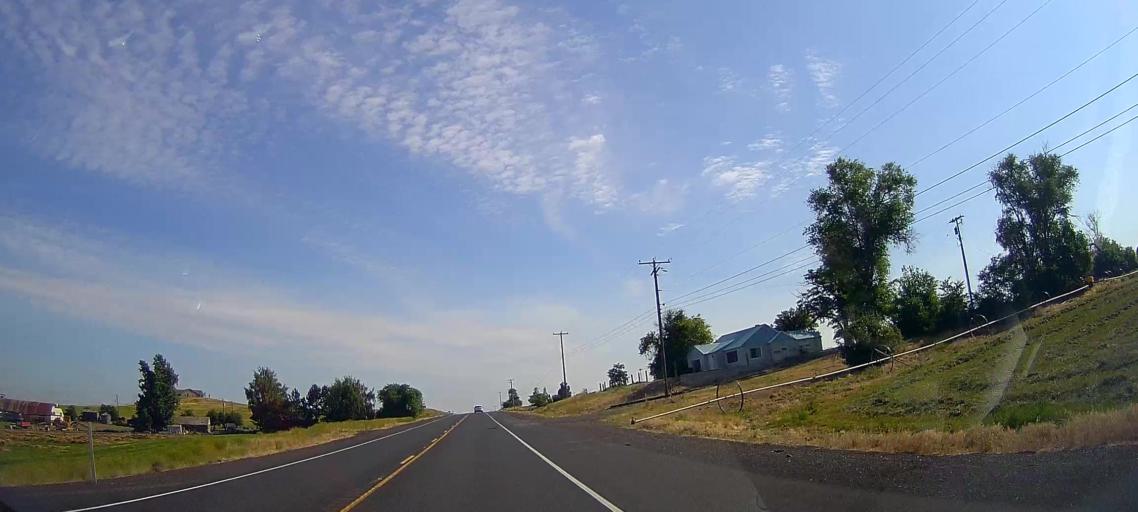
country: US
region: Oregon
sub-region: Jefferson County
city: Culver
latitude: 44.5293
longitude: -121.1781
